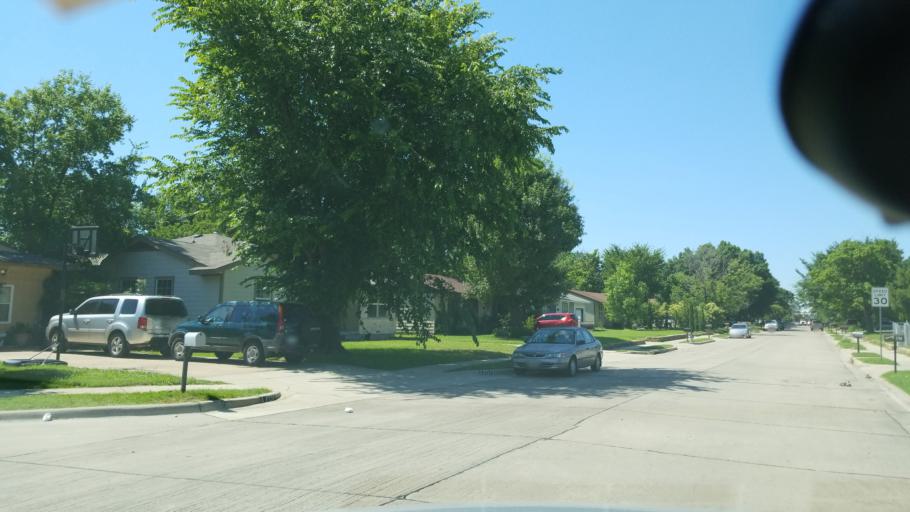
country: US
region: Texas
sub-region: Dallas County
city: Irving
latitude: 32.8315
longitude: -96.9364
